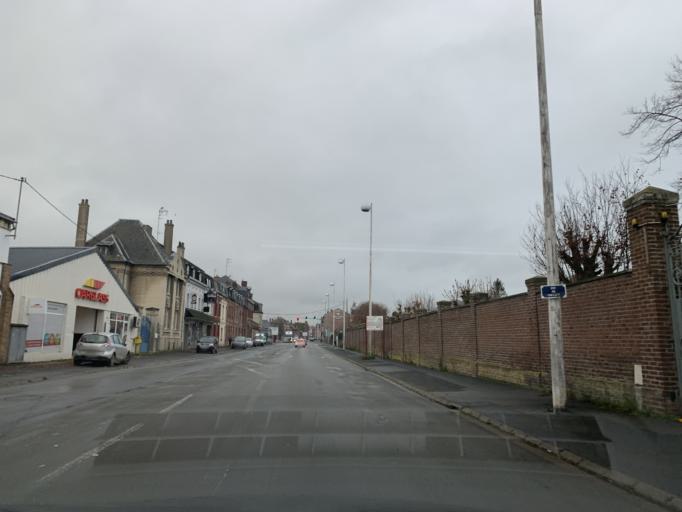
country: FR
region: Nord-Pas-de-Calais
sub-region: Departement du Nord
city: Neuville-Saint-Remy
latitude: 50.1771
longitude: 3.2200
